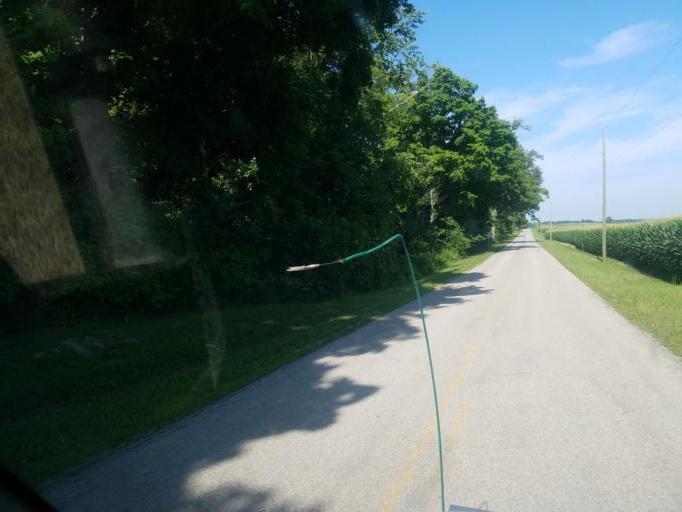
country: US
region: Ohio
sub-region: Logan County
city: Northwood
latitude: 40.5530
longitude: -83.6641
